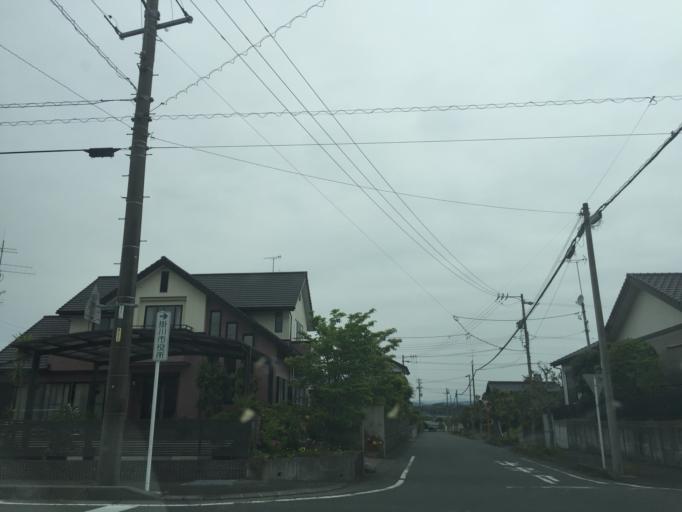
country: JP
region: Shizuoka
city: Kakegawa
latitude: 34.7662
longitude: 137.9933
